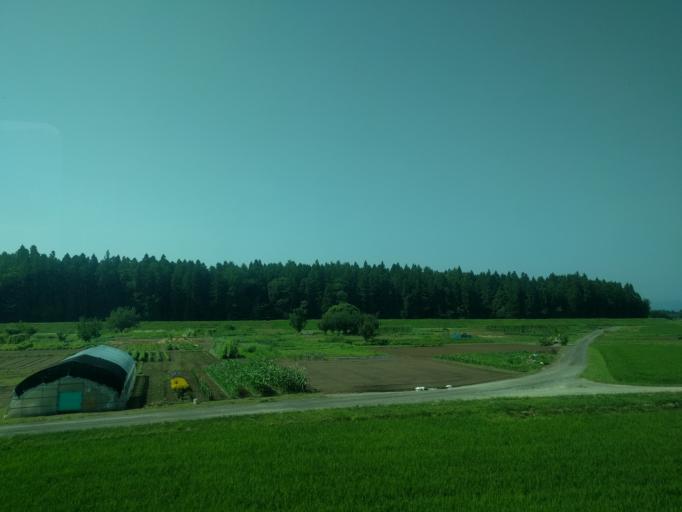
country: JP
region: Fukushima
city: Inawashiro
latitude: 37.5414
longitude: 140.1264
